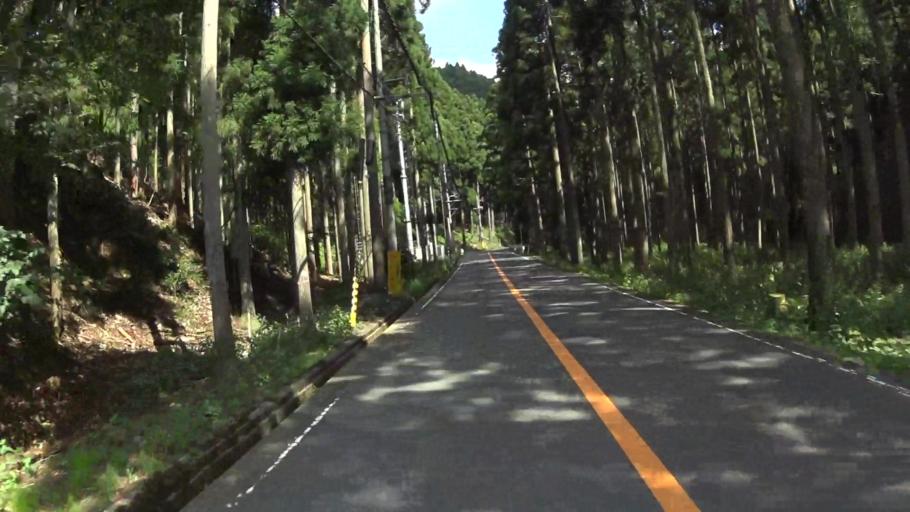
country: JP
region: Kyoto
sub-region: Kyoto-shi
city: Kamigyo-ku
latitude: 35.2485
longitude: 135.6491
